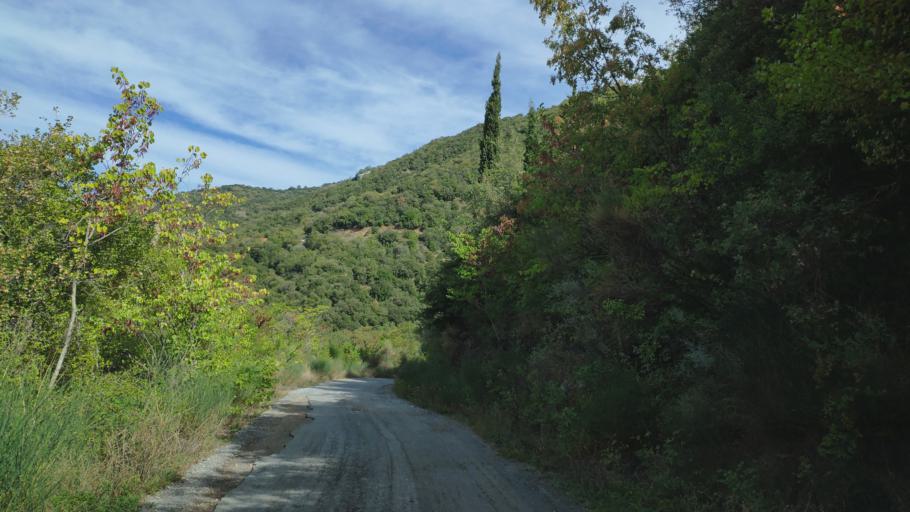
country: GR
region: Peloponnese
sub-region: Nomos Arkadias
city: Dimitsana
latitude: 37.5415
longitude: 22.0522
